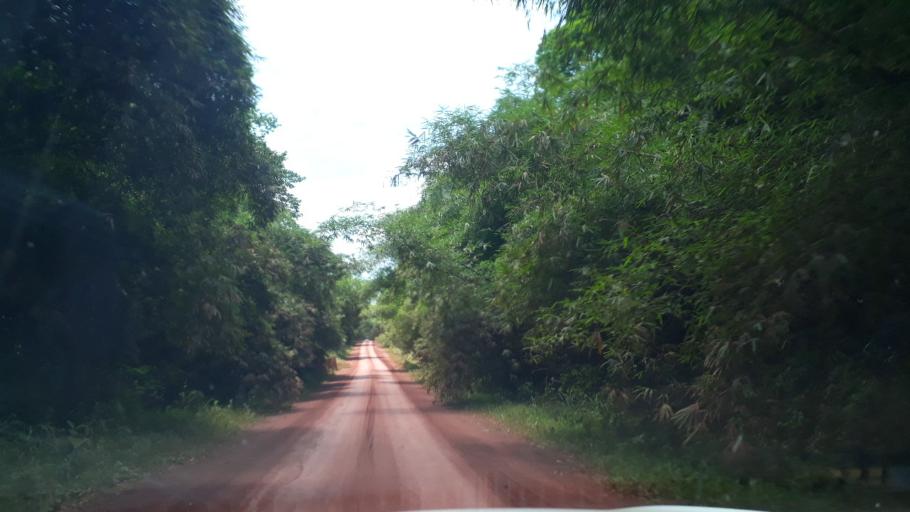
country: CD
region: Eastern Province
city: Kisangani
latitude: 0.5508
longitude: 25.8366
